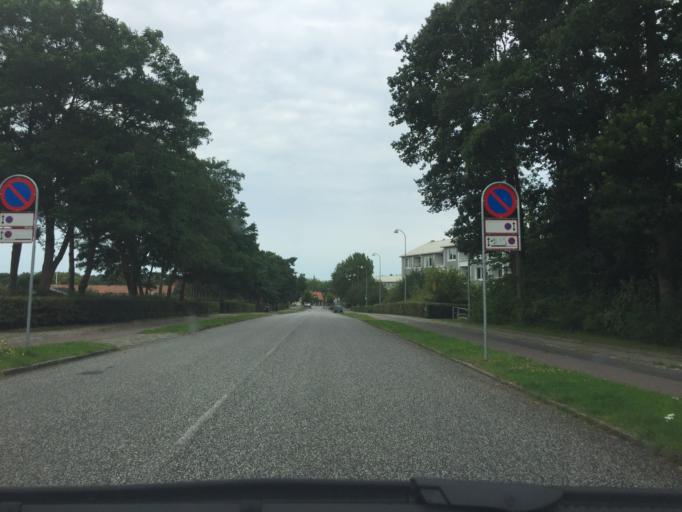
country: DK
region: Capital Region
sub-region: Lyngby-Tarbaek Kommune
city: Kongens Lyngby
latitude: 55.7942
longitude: 12.5217
